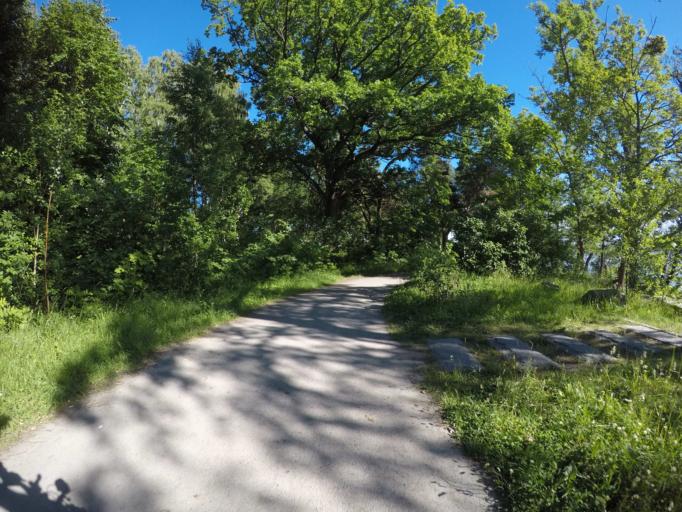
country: SE
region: Vaestmanland
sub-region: Vasteras
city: Vasteras
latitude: 59.6033
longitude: 16.5694
